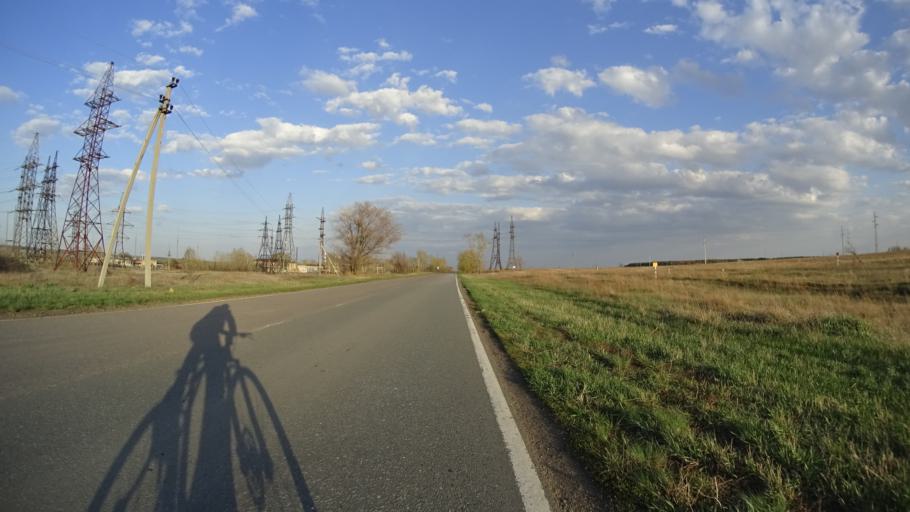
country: RU
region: Chelyabinsk
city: Troitsk
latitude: 54.0578
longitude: 61.5828
